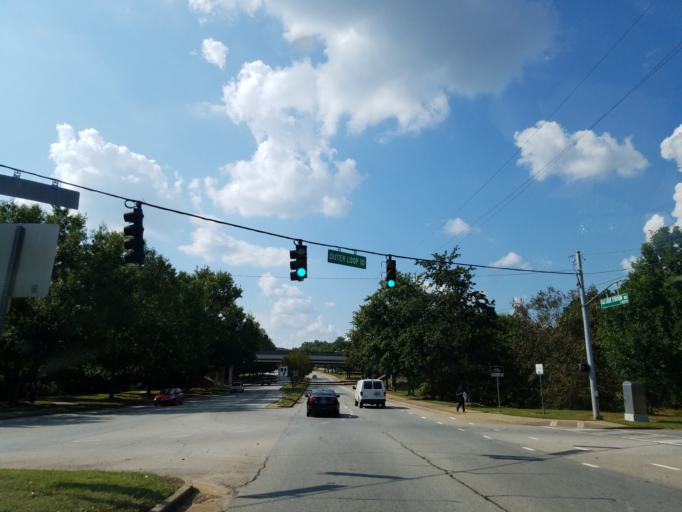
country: US
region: Georgia
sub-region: Clarke County
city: Athens
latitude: 33.9326
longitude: -83.3658
